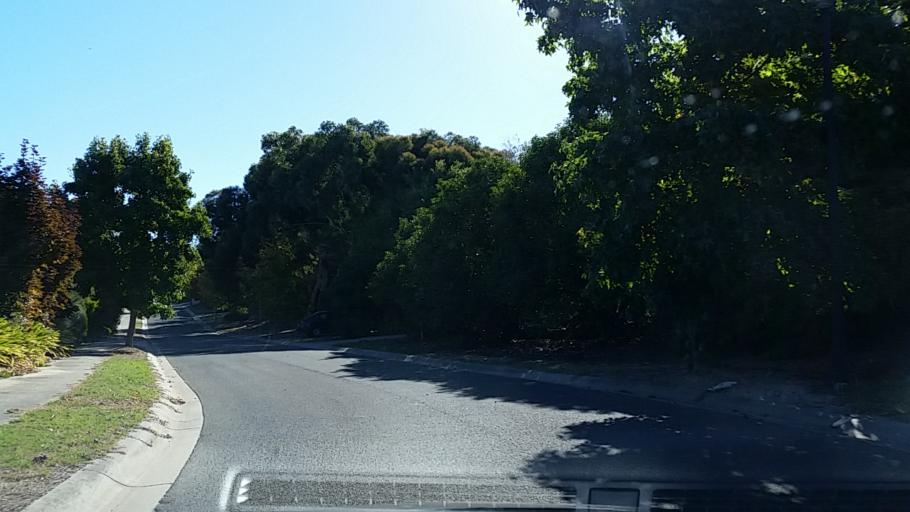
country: AU
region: South Australia
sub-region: Mount Barker
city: Mount Barker
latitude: -35.0610
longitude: 138.8841
